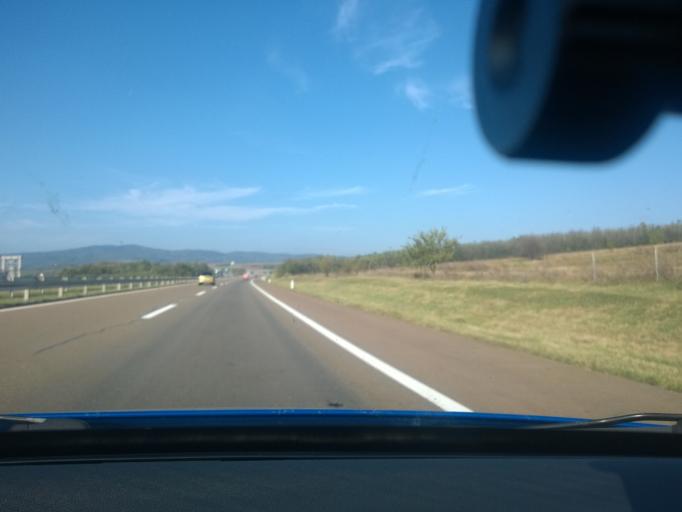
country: RS
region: Central Serbia
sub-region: Nisavski Okrug
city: Razanj
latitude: 43.6145
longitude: 21.5973
